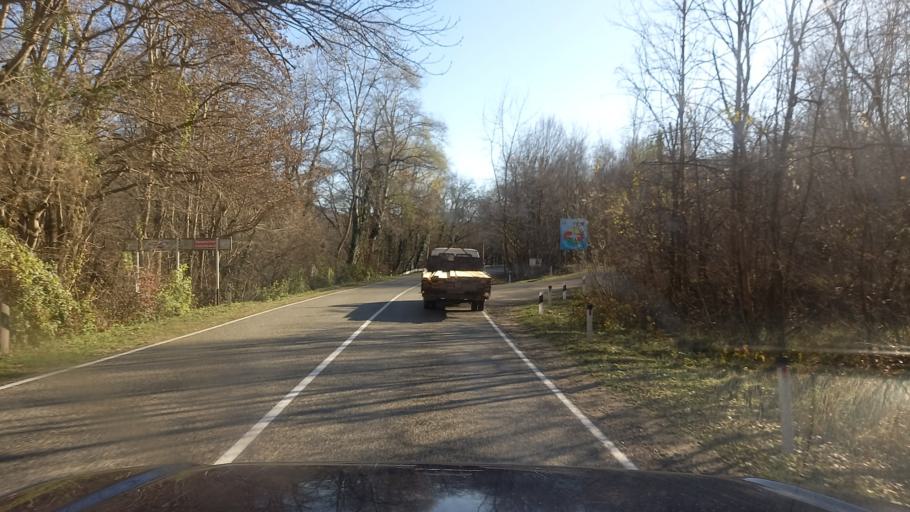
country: RU
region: Krasnodarskiy
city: Goryachiy Klyuch
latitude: 44.6063
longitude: 39.0807
